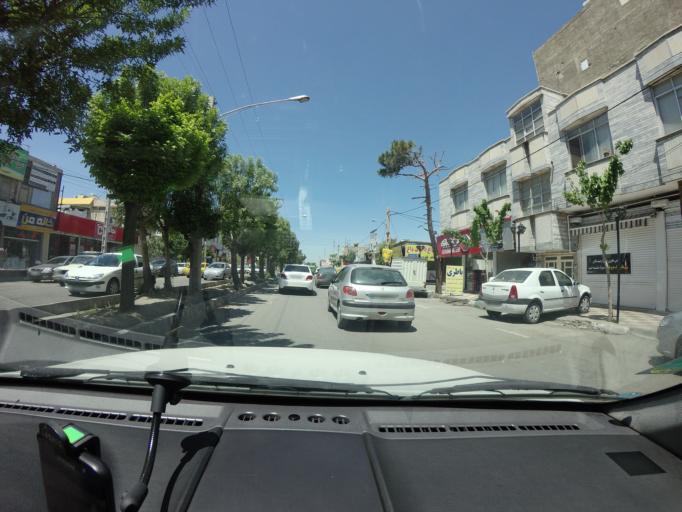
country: IR
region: Tehran
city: Eslamshahr
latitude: 35.5333
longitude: 51.2181
